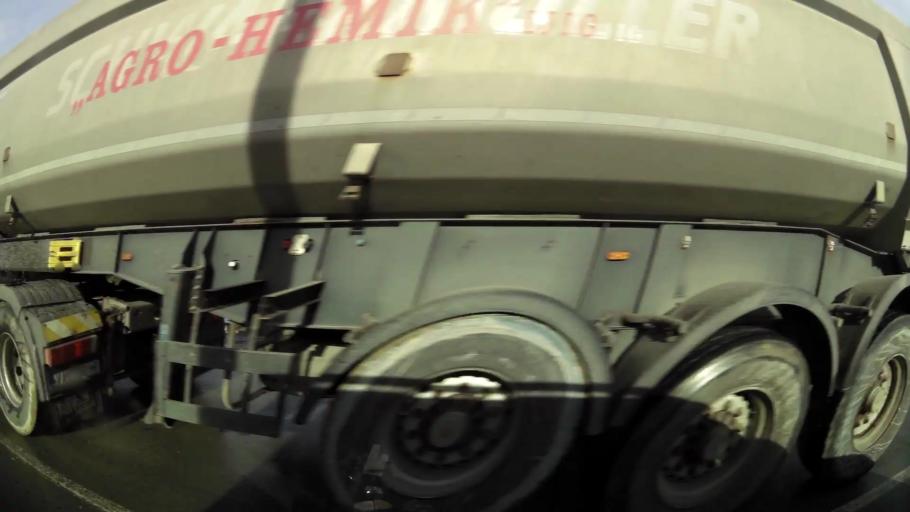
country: RS
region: Central Serbia
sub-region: Belgrade
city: Rakovica
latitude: 44.7267
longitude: 20.4369
